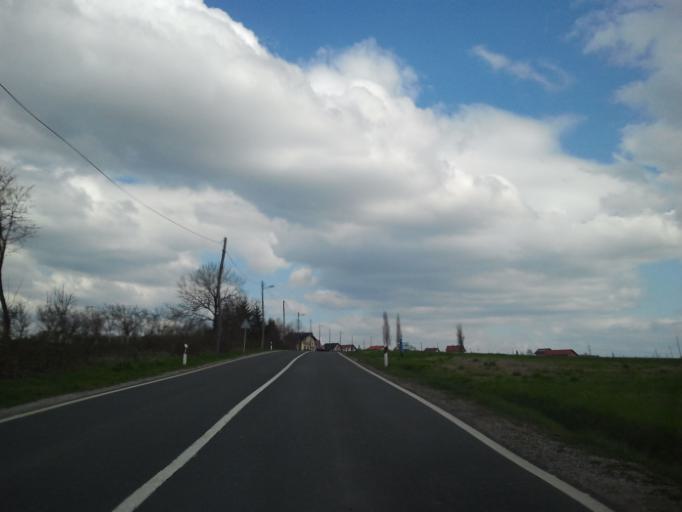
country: HR
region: Grad Zagreb
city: Horvati
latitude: 45.7032
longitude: 15.7706
